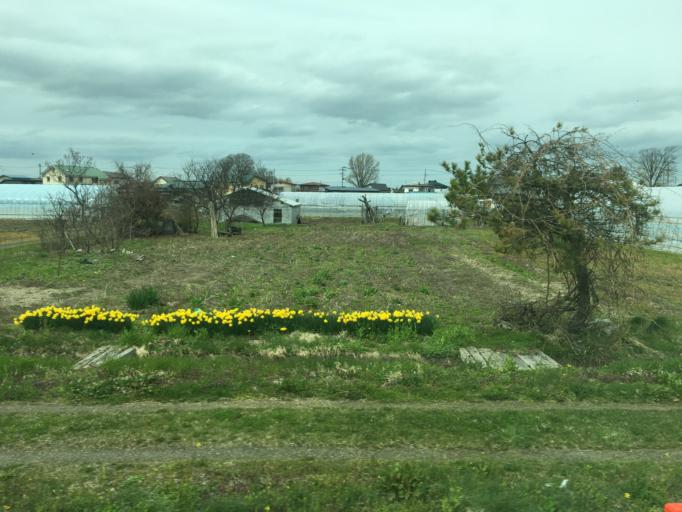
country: JP
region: Aomori
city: Shimokizukuri
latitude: 40.7950
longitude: 140.3768
